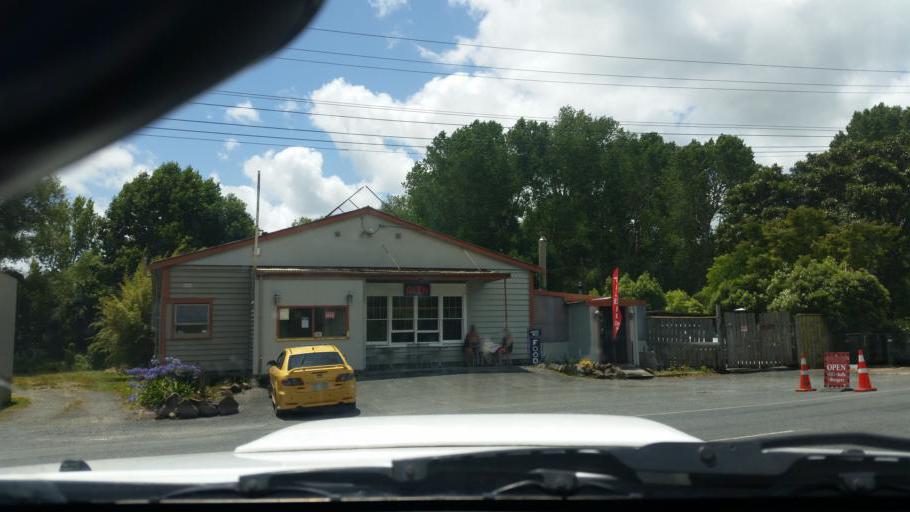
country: NZ
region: Northland
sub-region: Whangarei
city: Ruakaka
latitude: -36.1000
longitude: 174.2354
